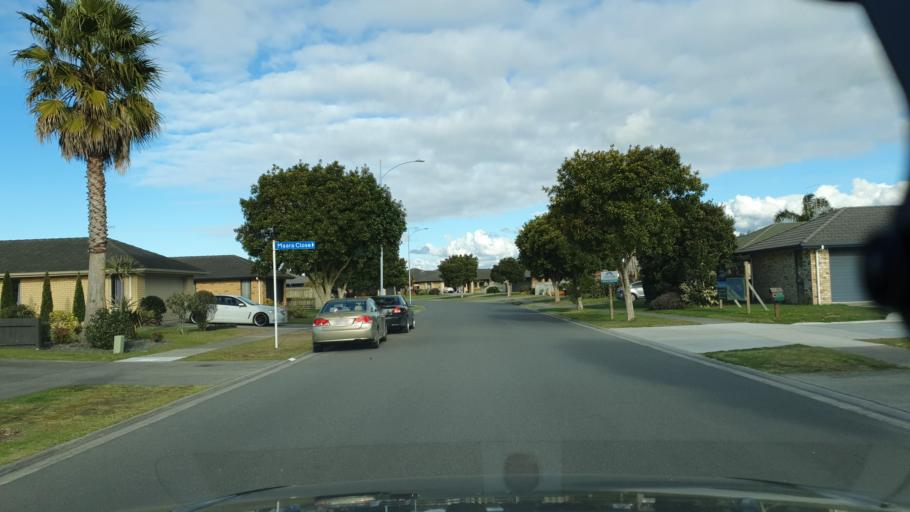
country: NZ
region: Bay of Plenty
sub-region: Tauranga City
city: Tauranga
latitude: -37.7086
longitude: 176.2905
